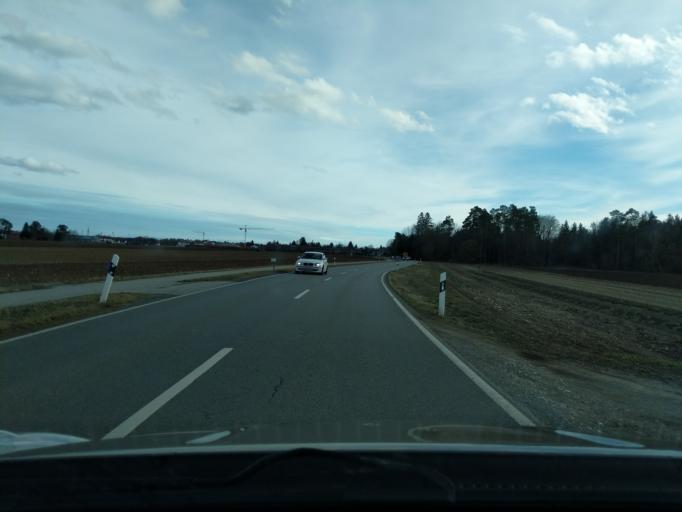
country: DE
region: Bavaria
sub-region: Upper Bavaria
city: Vaterstetten
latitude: 48.1210
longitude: 11.7669
